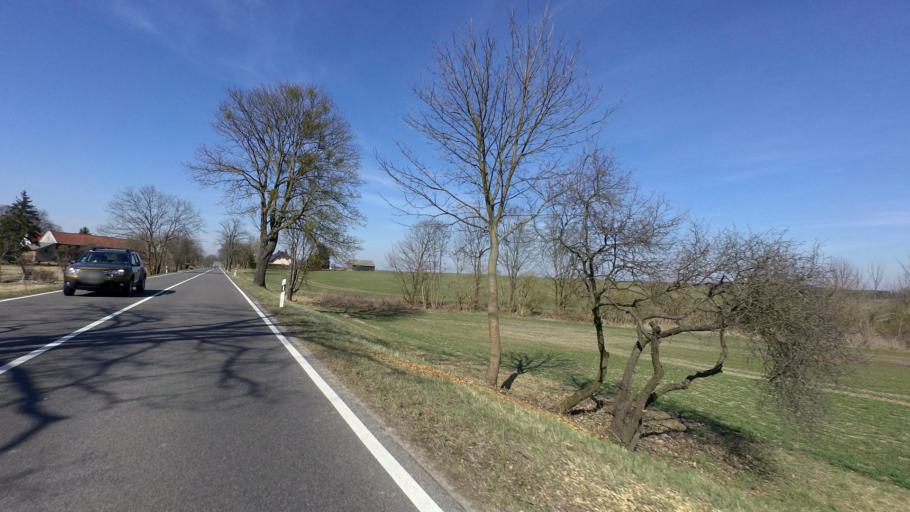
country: DE
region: Brandenburg
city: Protzel
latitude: 52.5991
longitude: 14.0250
